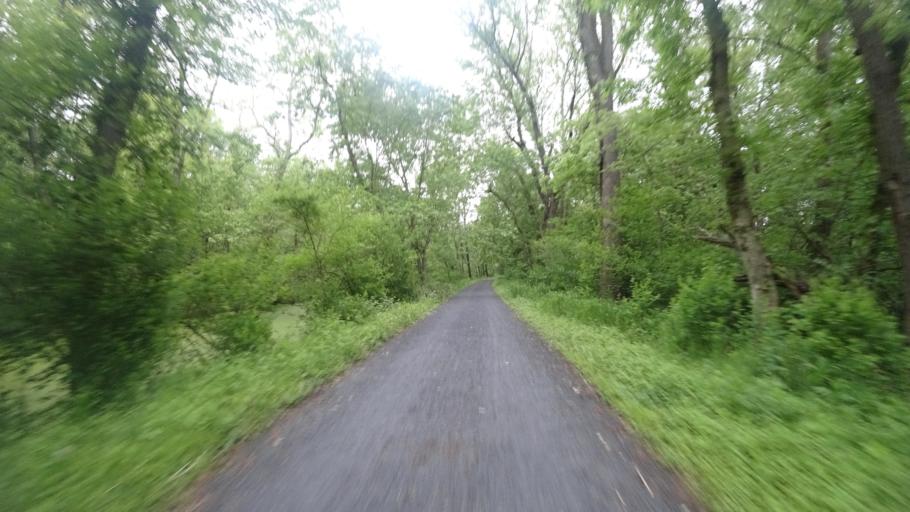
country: US
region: Maryland
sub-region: Frederick County
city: Brunswick
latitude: 39.3290
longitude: -77.6729
